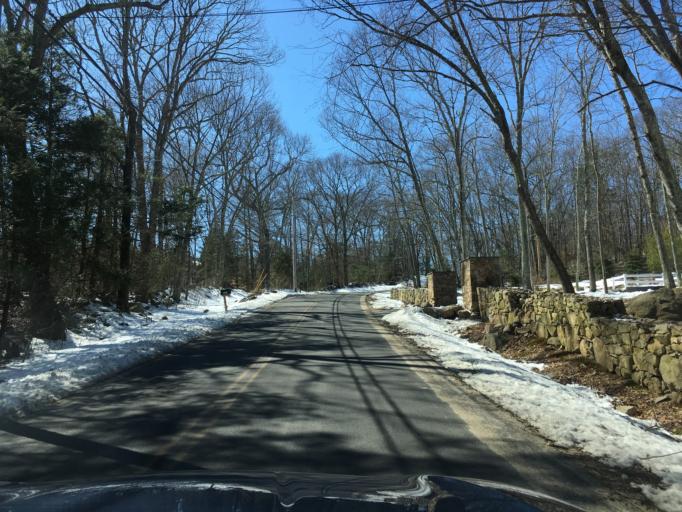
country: US
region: Rhode Island
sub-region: Washington County
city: Exeter
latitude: 41.6084
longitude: -71.5088
